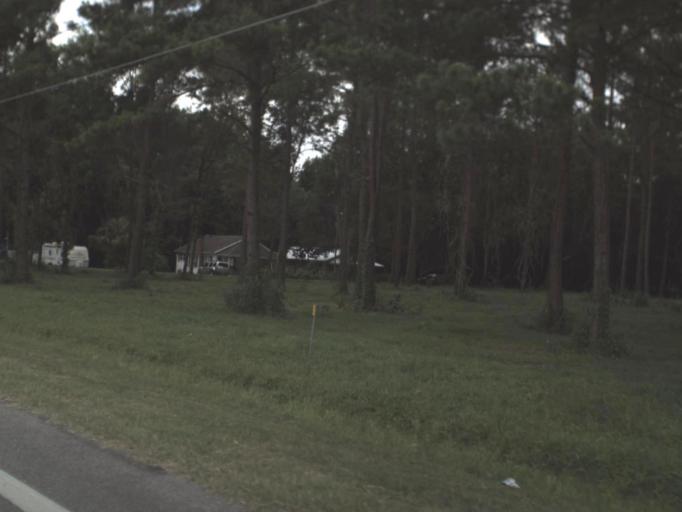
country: US
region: Florida
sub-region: Hamilton County
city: Jasper
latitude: 30.5093
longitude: -82.9463
